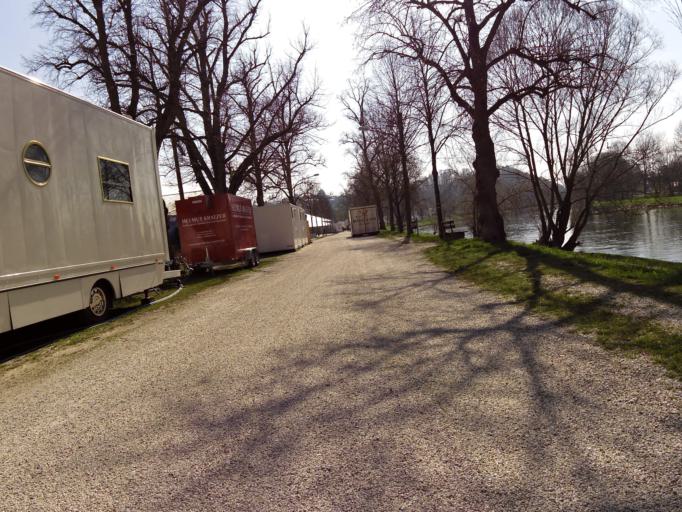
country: DE
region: Bavaria
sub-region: Lower Bavaria
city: Landshut
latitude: 48.5308
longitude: 12.1435
